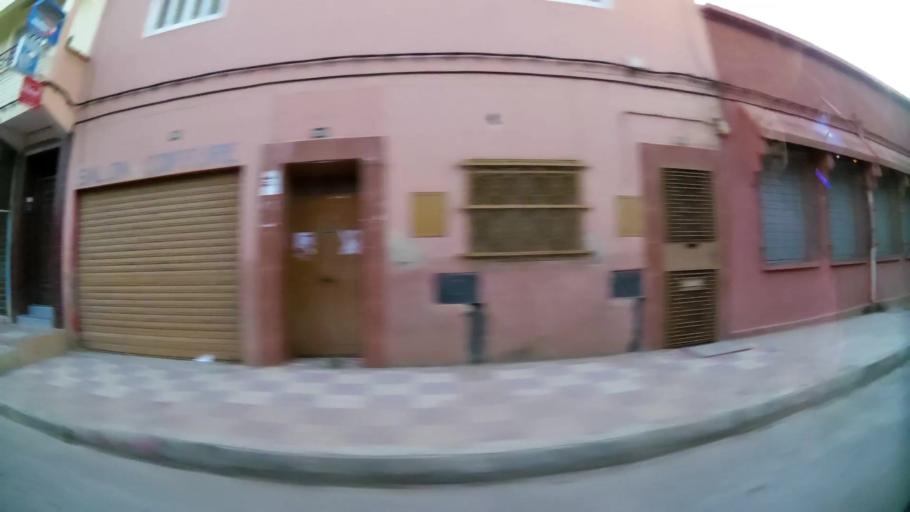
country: MA
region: Oriental
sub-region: Berkane-Taourirt
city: Berkane
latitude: 34.9224
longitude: -2.3297
